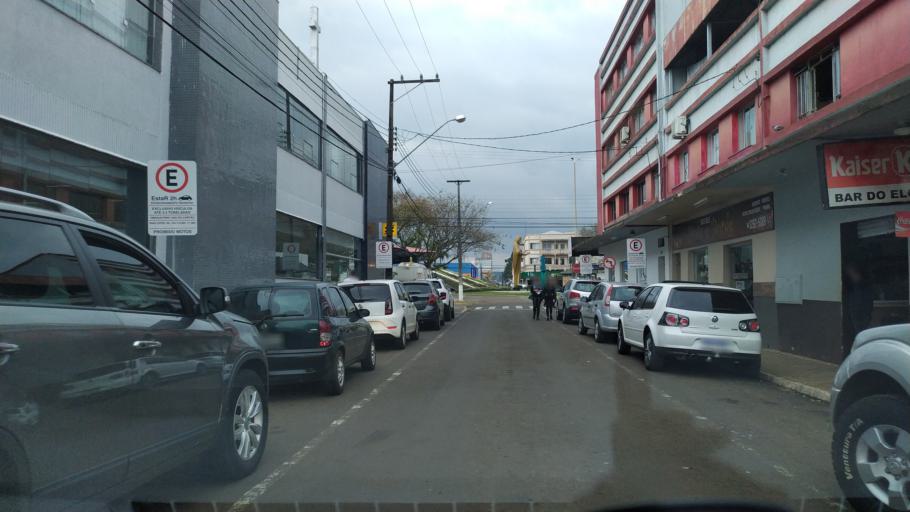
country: BR
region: Parana
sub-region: Palmas
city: Palmas
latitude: -26.4829
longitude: -51.9915
